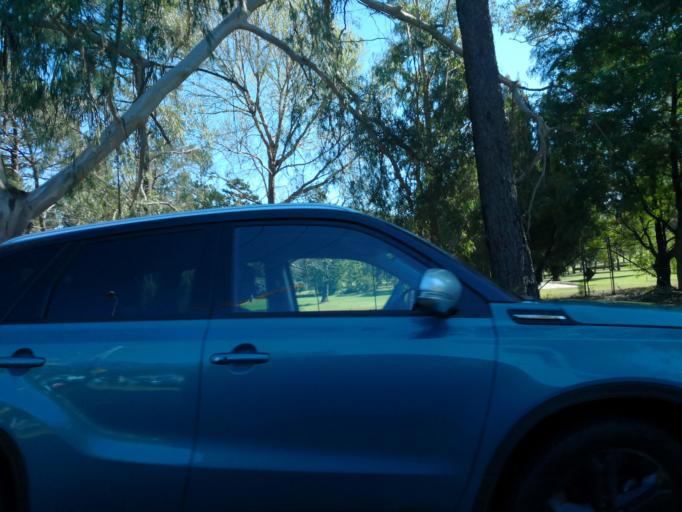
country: AU
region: New South Wales
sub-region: Gosford Shire
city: Gosford
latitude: -33.4199
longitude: 151.3369
